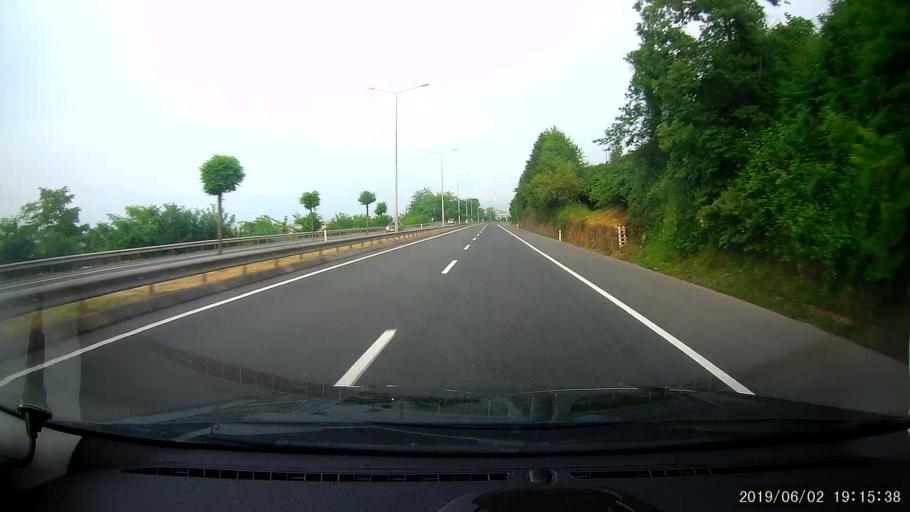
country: TR
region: Giresun
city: Piraziz
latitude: 40.9618
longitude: 38.1002
